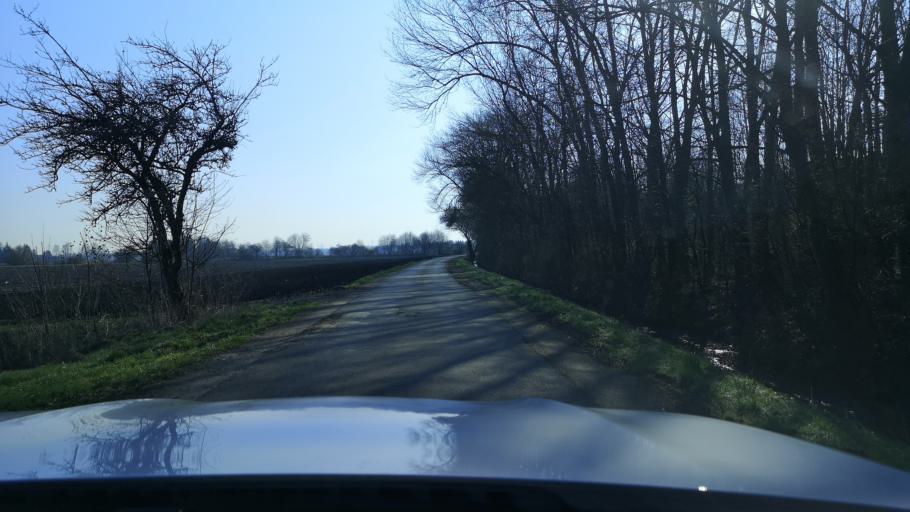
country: DE
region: Bavaria
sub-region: Upper Bavaria
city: Pliening
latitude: 48.2259
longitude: 11.7752
